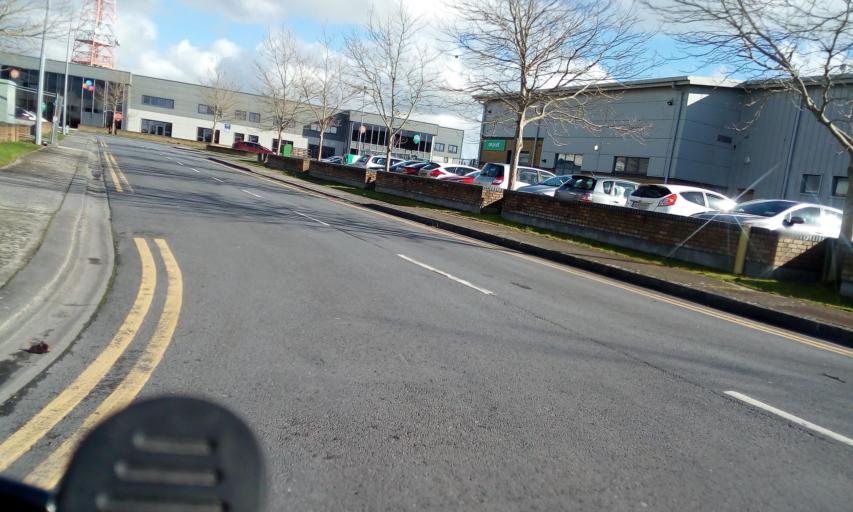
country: IE
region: Leinster
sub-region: Kilkenny
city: Kilkenny
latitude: 52.6524
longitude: -7.2319
